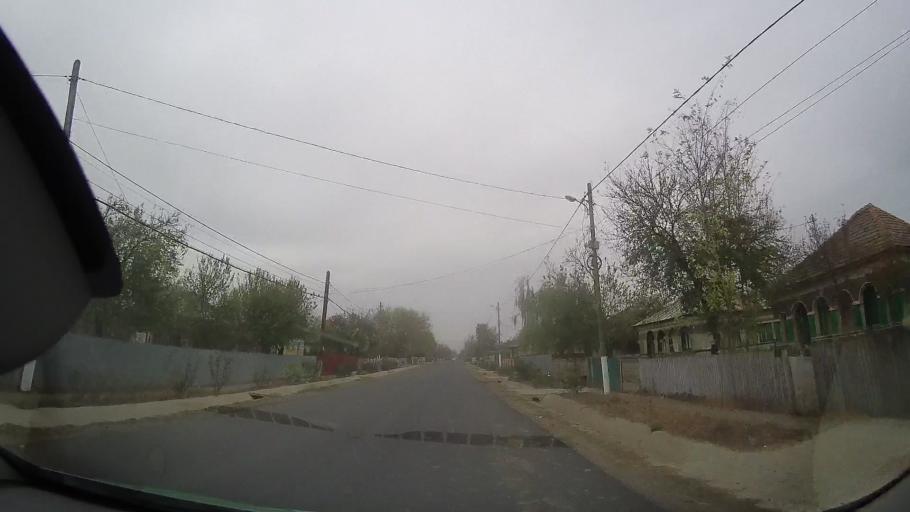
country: RO
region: Braila
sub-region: Comuna Rosiori
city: Rosiori
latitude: 44.8081
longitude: 27.3848
